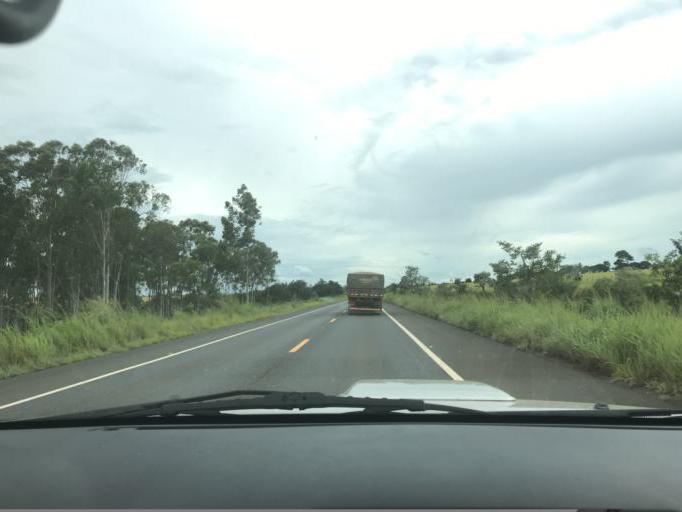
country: BR
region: Minas Gerais
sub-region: Araxa
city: Araxa
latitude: -19.3756
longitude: -46.8576
